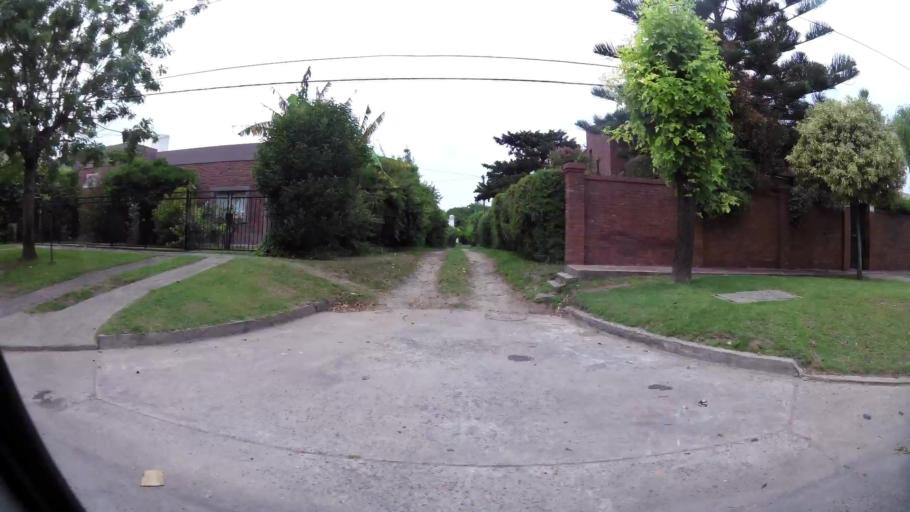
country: AR
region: Buenos Aires
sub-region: Partido de La Plata
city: La Plata
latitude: -34.9022
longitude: -57.9824
